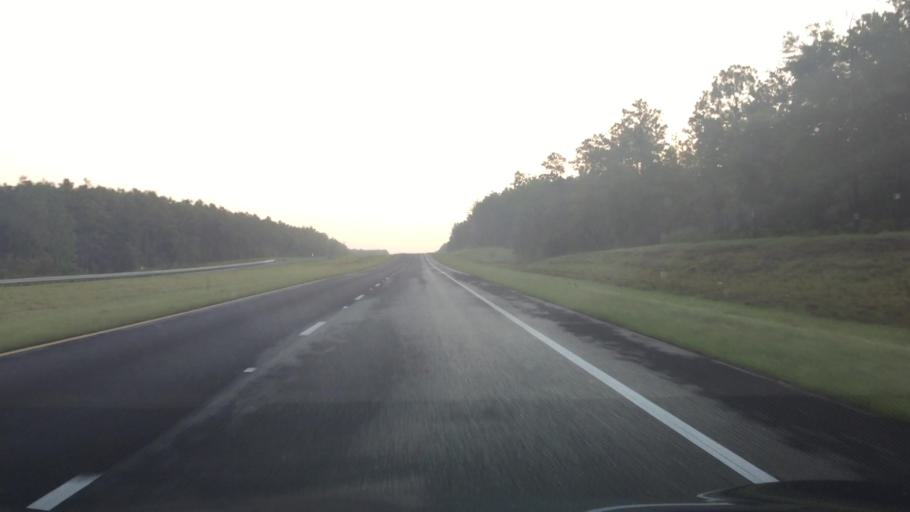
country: US
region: Florida
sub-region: Walton County
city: Freeport
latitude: 30.5038
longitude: -86.1158
